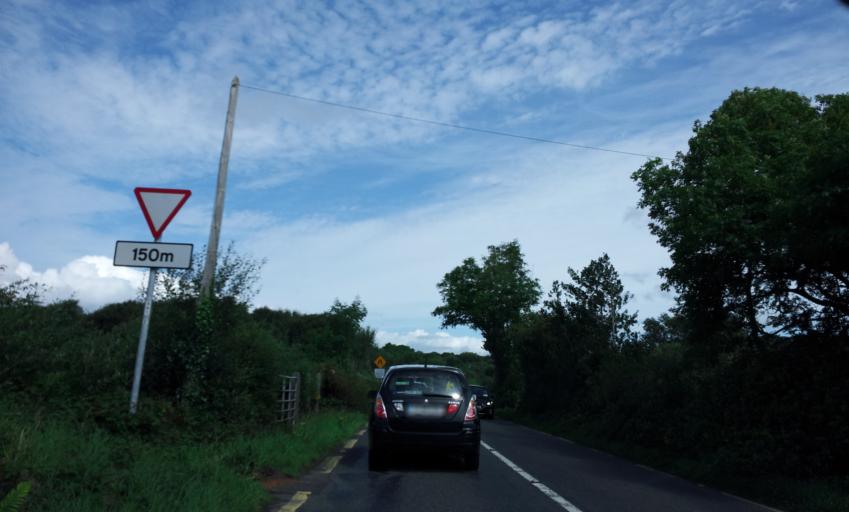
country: IE
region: Munster
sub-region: Ciarrai
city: Killorglin
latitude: 52.0673
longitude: -9.9062
